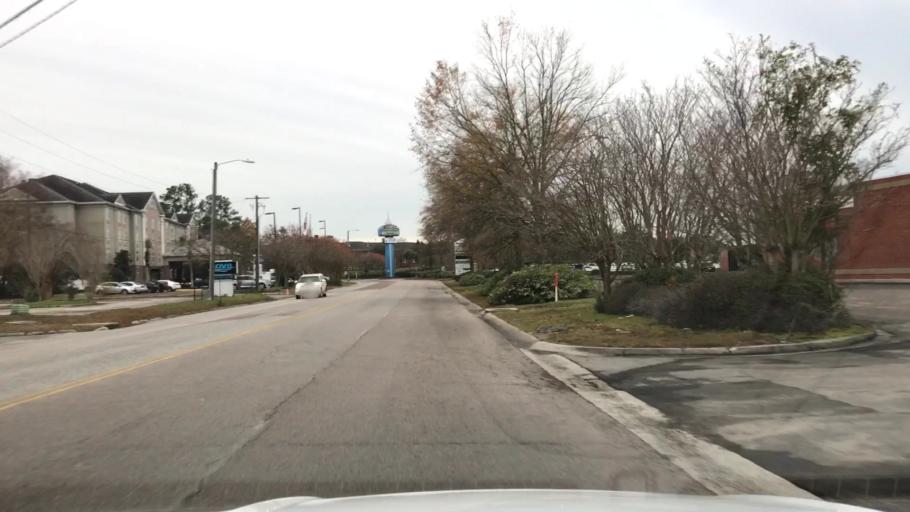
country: US
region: South Carolina
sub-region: Berkeley County
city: Hanahan
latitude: 32.9420
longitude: -80.0459
